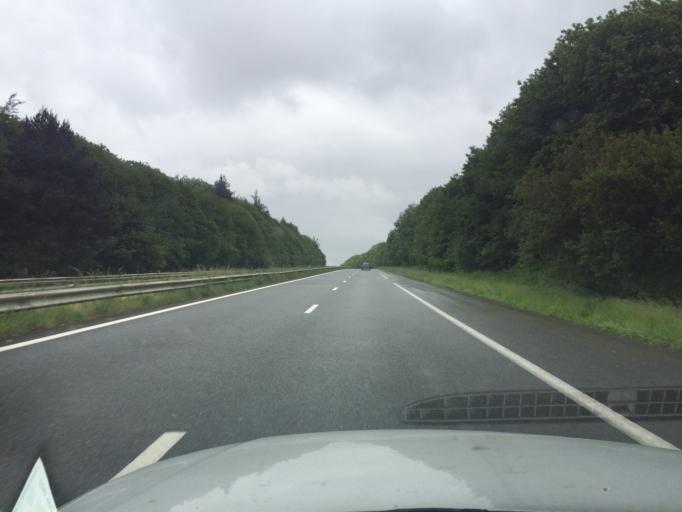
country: FR
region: Brittany
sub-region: Departement du Finistere
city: Plouigneau
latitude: 48.5742
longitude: -3.6888
